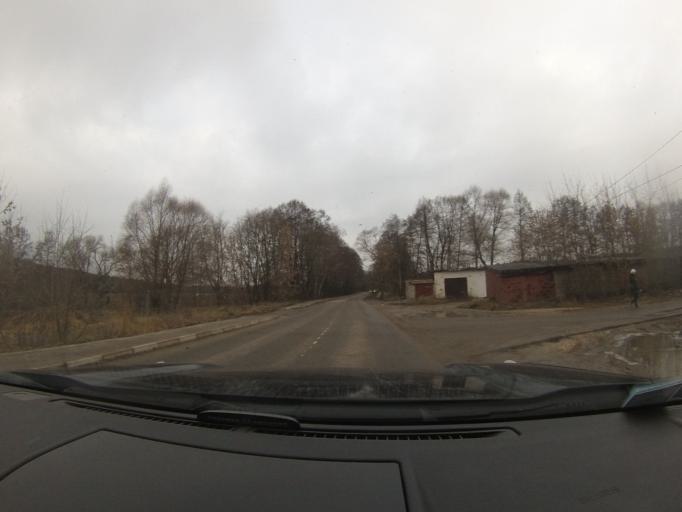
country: RU
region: Moskovskaya
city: Peski
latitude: 55.2621
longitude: 38.7621
